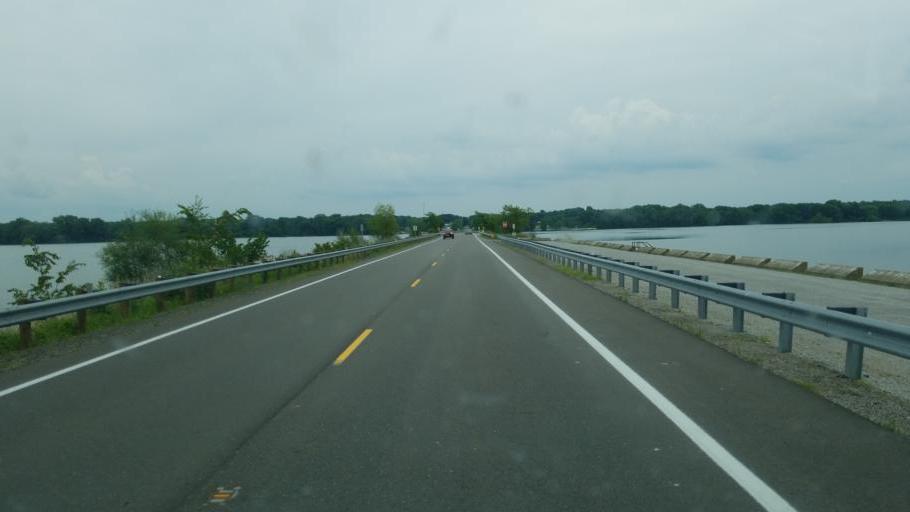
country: US
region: Ohio
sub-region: Trumbull County
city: Cortland
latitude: 41.3899
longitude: -80.7522
